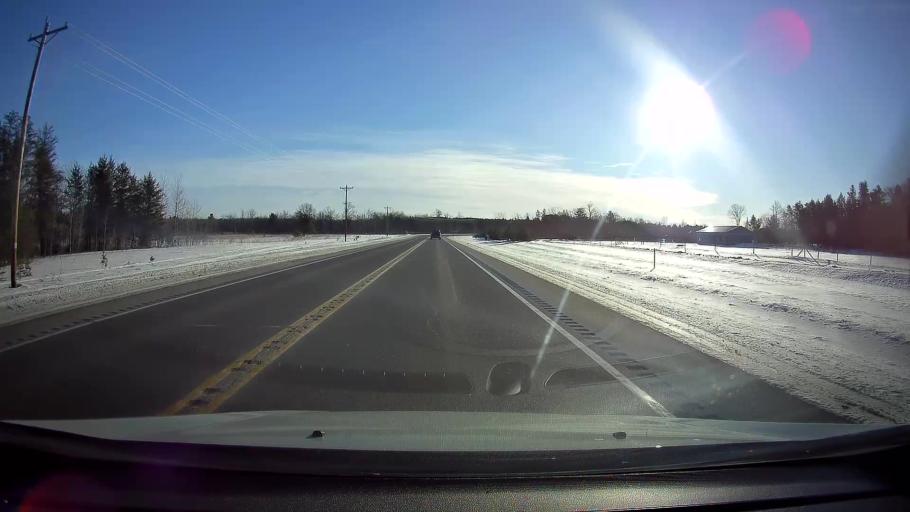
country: US
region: Wisconsin
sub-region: Sawyer County
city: Hayward
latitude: 45.9963
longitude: -91.5977
